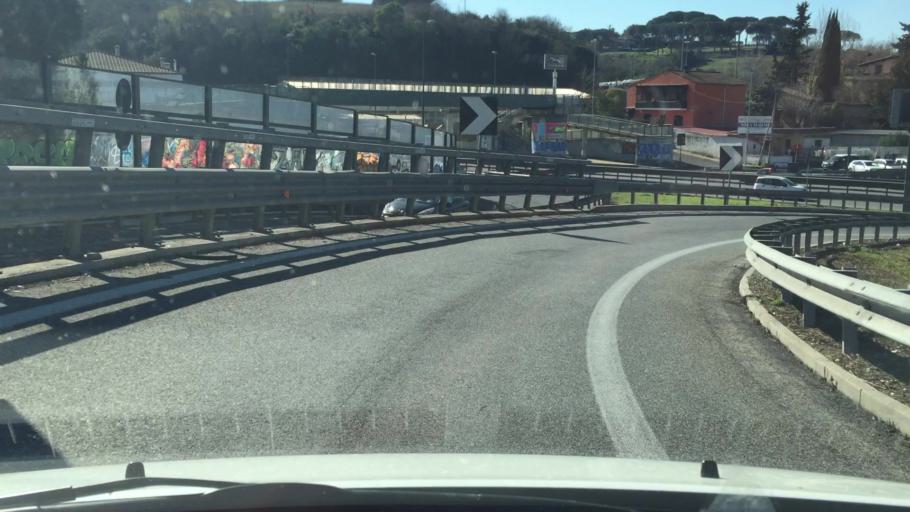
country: IT
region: Latium
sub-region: Citta metropolitana di Roma Capitale
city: Monte Caminetto
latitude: 41.9852
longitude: 12.4937
